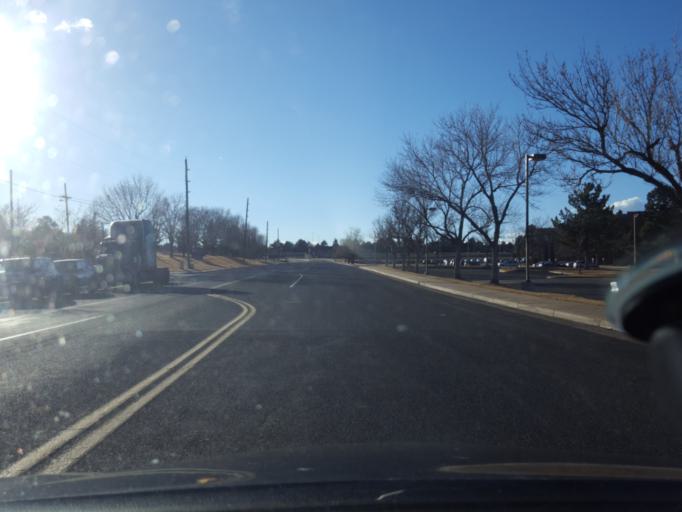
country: US
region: Colorado
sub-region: Adams County
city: Aurora
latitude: 39.7220
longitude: -104.8207
